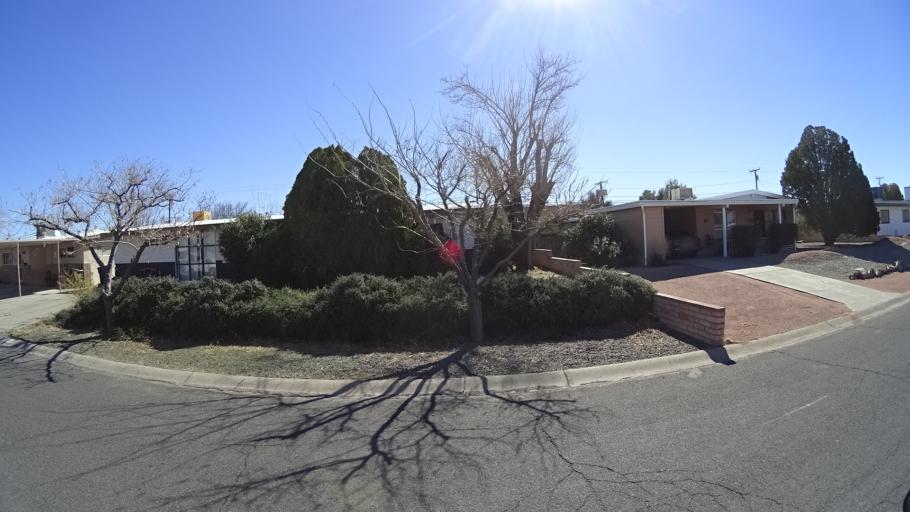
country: US
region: Arizona
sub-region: Mohave County
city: Kingman
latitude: 35.2120
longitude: -114.0183
